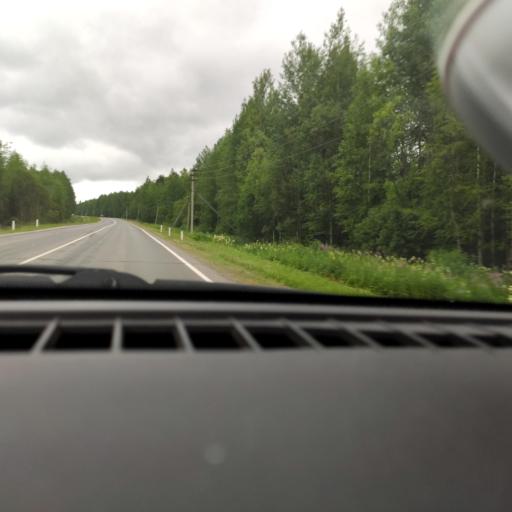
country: RU
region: Perm
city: Polazna
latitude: 58.2933
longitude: 56.1623
